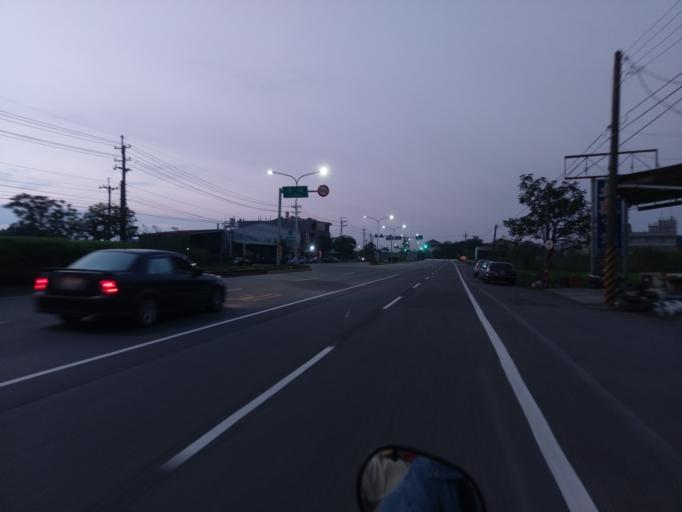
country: TW
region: Taiwan
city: Xinying
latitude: 23.1929
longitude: 120.3247
